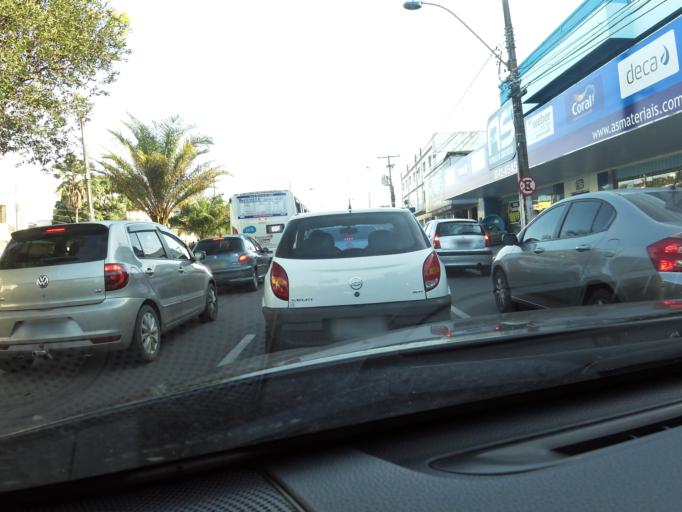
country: BR
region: Espirito Santo
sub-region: Vila Velha
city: Vila Velha
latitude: -20.3464
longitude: -40.2935
